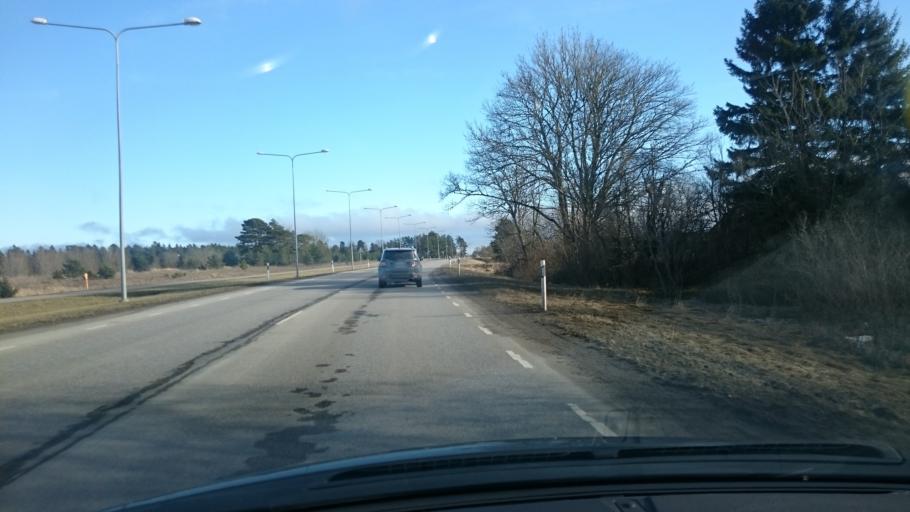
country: EE
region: Harju
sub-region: Harku vald
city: Tabasalu
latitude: 59.4416
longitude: 24.4926
